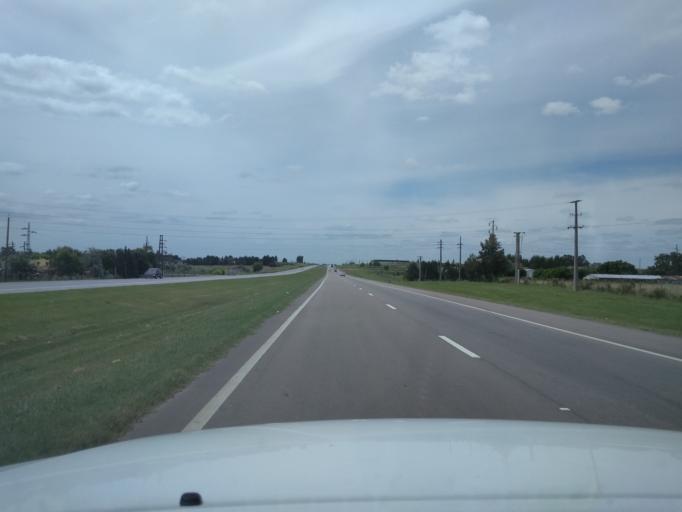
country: UY
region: Canelones
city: Las Piedras
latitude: -34.7133
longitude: -56.2433
